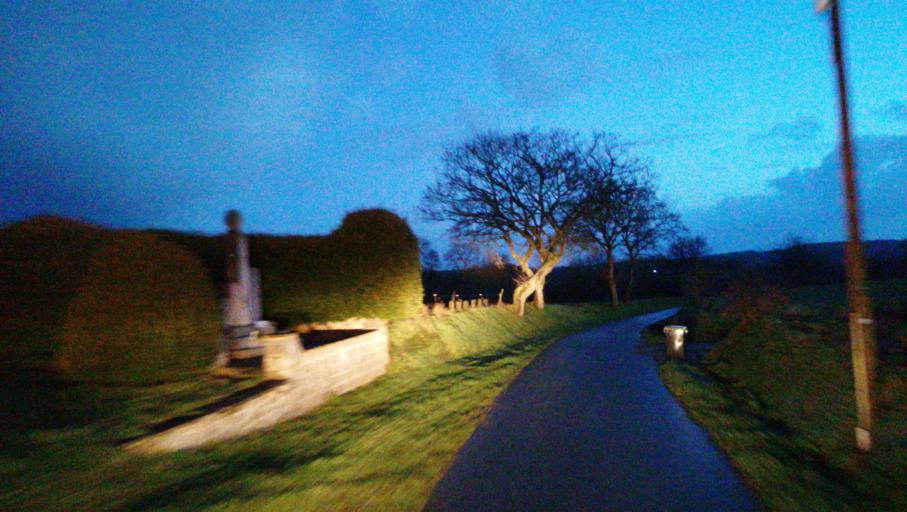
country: FR
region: Brittany
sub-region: Departement des Cotes-d'Armor
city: Plehedel
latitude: 48.6683
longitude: -3.0516
